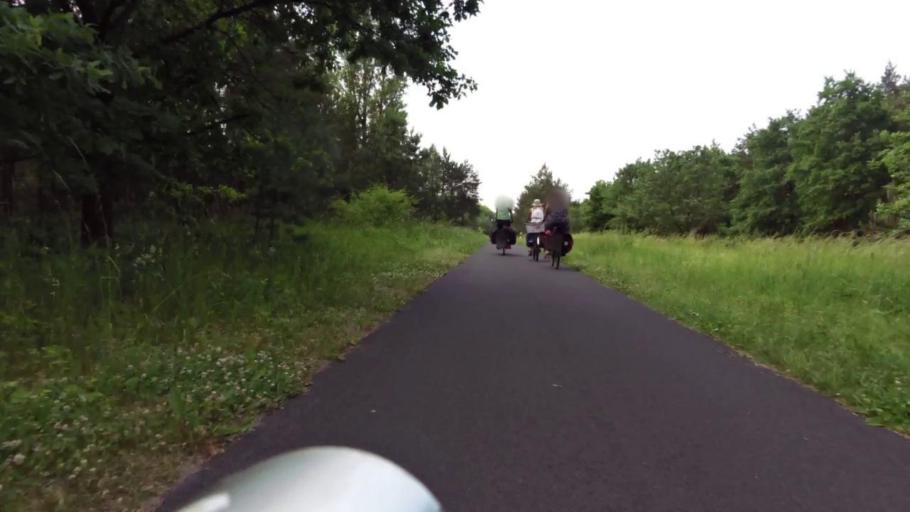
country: PL
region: Kujawsko-Pomorskie
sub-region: Powiat torunski
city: Lysomice
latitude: 53.0767
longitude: 18.5421
